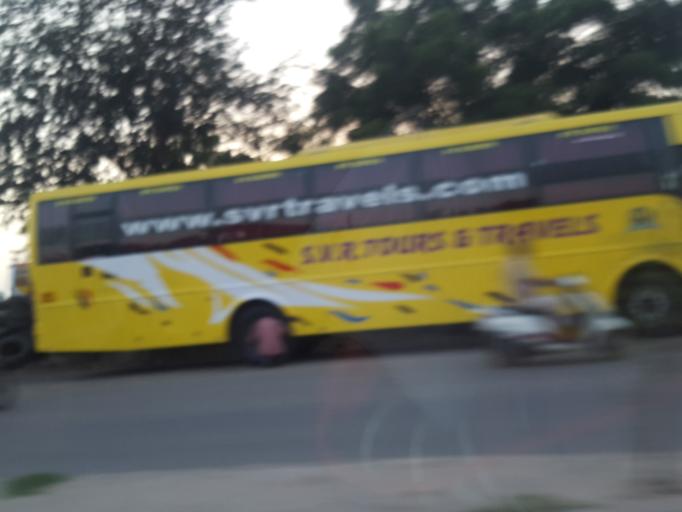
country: IN
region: Telangana
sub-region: Medak
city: Serilingampalle
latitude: 17.5331
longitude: 78.3569
